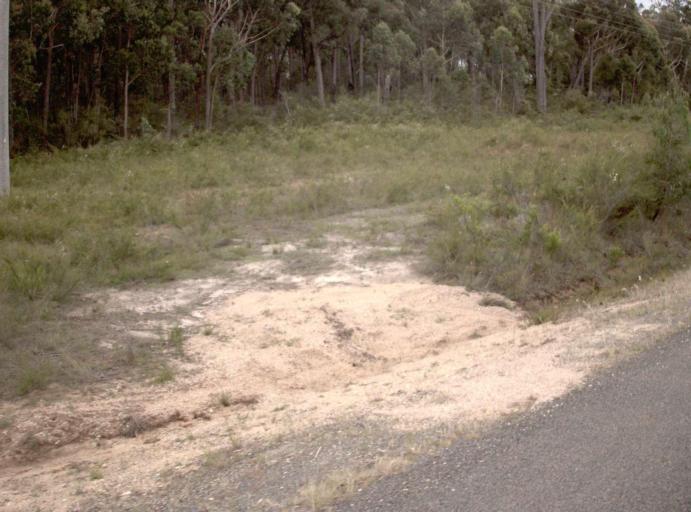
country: AU
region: Victoria
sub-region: East Gippsland
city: Lakes Entrance
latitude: -37.7179
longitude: 147.9595
